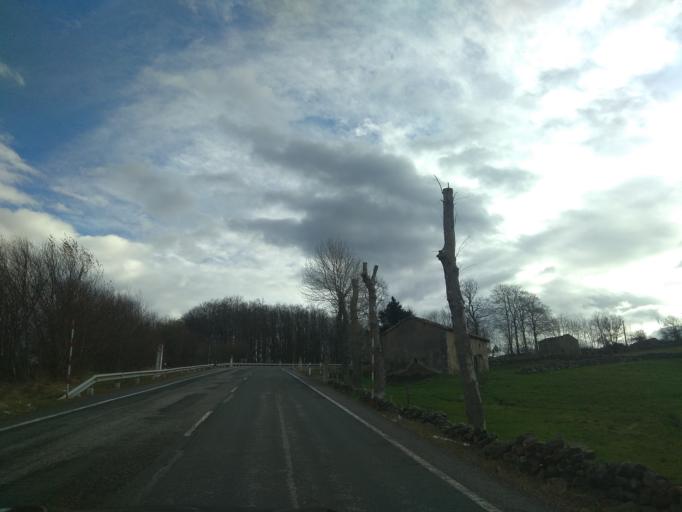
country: ES
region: Cantabria
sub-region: Provincia de Cantabria
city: San Pedro del Romeral
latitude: 43.0708
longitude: -3.8850
